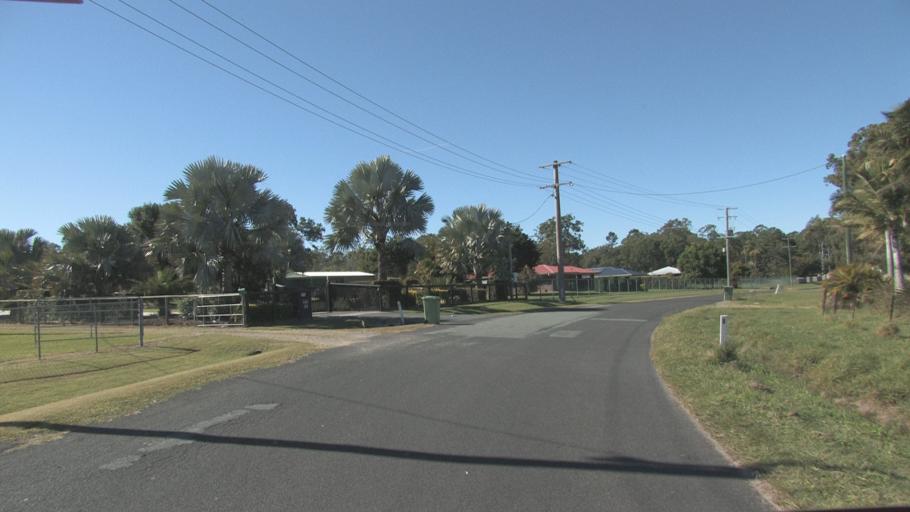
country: AU
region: Queensland
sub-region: Logan
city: Park Ridge South
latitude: -27.7227
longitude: 153.0345
